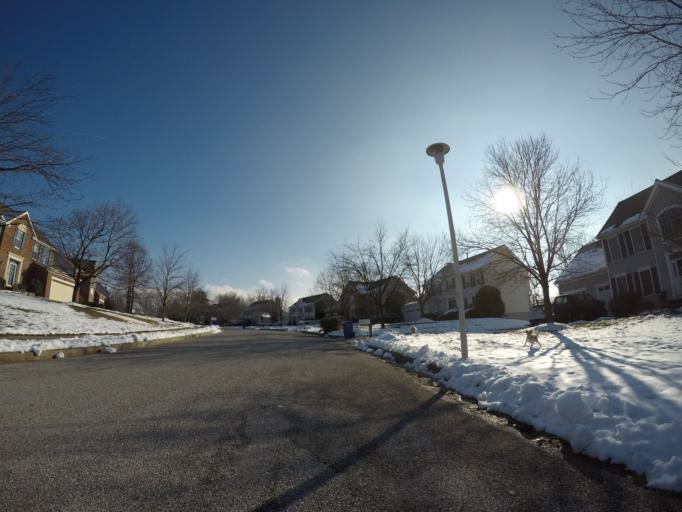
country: US
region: Maryland
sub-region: Howard County
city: Ilchester
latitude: 39.2174
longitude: -76.7770
